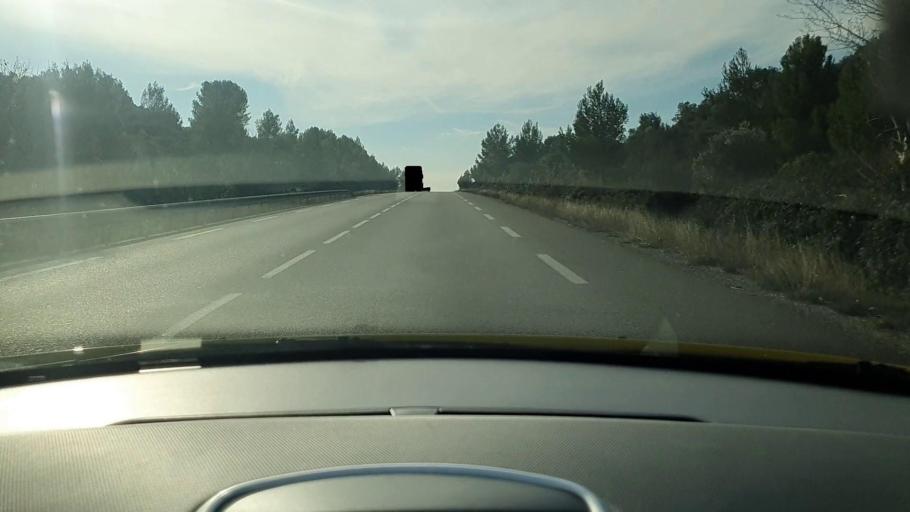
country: FR
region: Languedoc-Roussillon
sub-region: Departement du Gard
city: Comps
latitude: 43.8254
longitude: 4.6136
